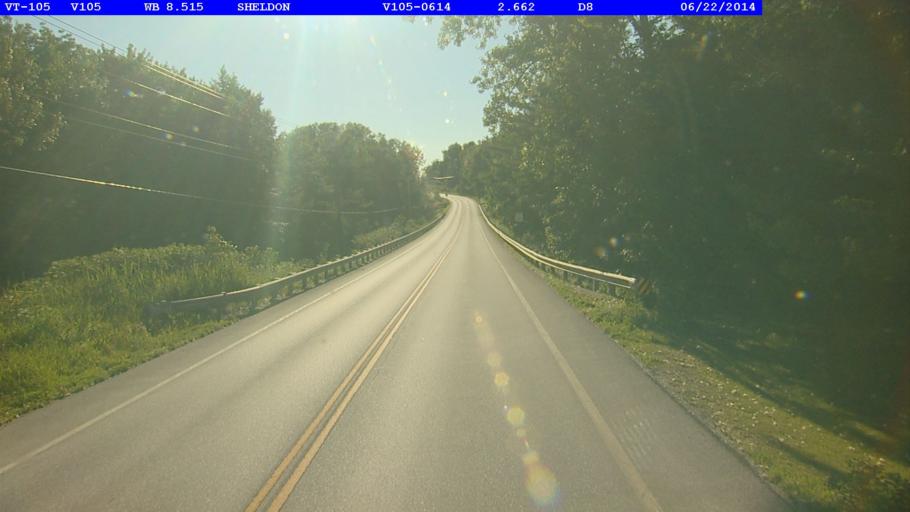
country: US
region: Vermont
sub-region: Franklin County
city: Saint Albans
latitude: 44.9043
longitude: -72.9790
